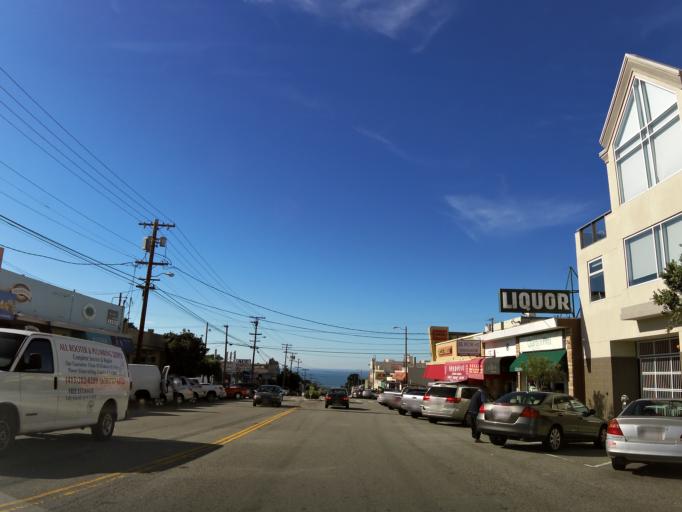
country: US
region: California
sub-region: San Mateo County
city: Daly City
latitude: 37.7537
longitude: -122.4896
